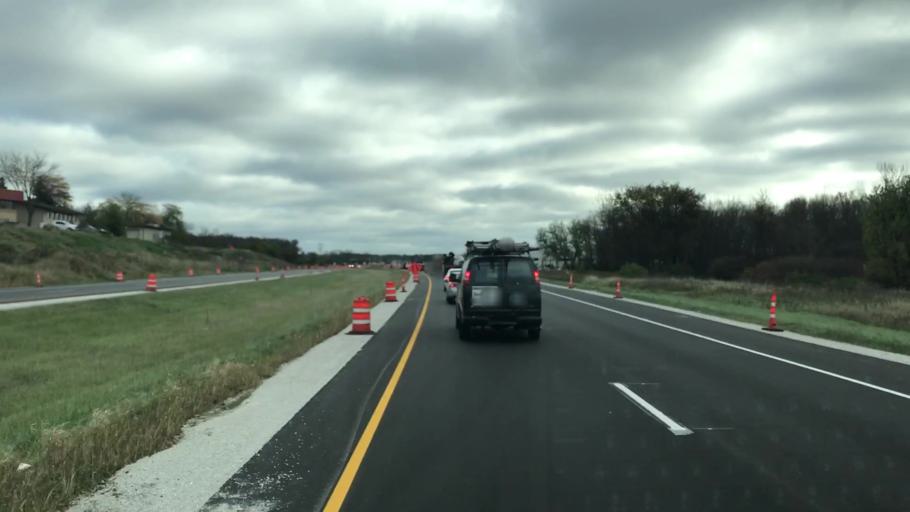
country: US
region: Wisconsin
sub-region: Waukesha County
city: Lannon
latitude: 43.0842
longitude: -88.1740
